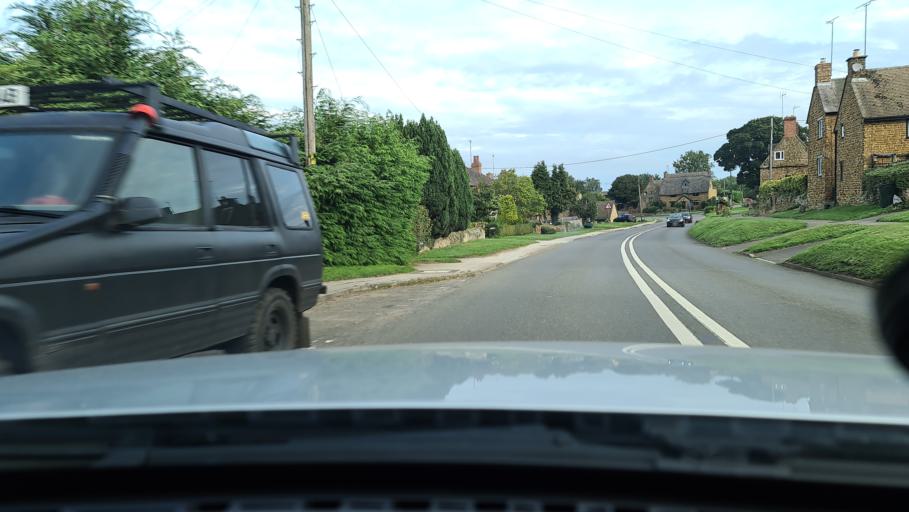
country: GB
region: England
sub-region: Oxfordshire
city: Hanwell
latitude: 52.0726
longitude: -1.3752
